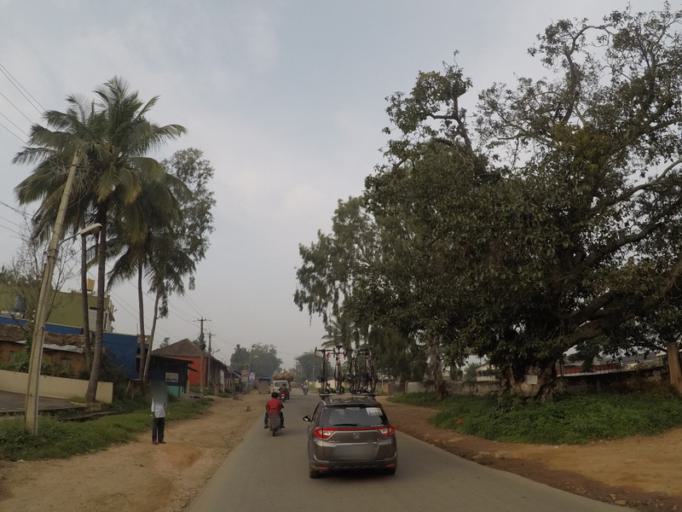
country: IN
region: Karnataka
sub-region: Chikmagalur
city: Chikmagalur
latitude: 13.2979
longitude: 75.7592
